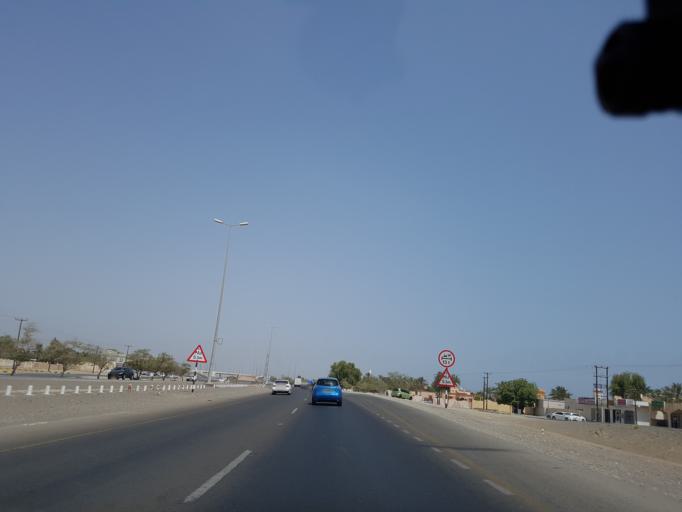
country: OM
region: Al Batinah
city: Saham
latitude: 24.1993
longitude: 56.8576
